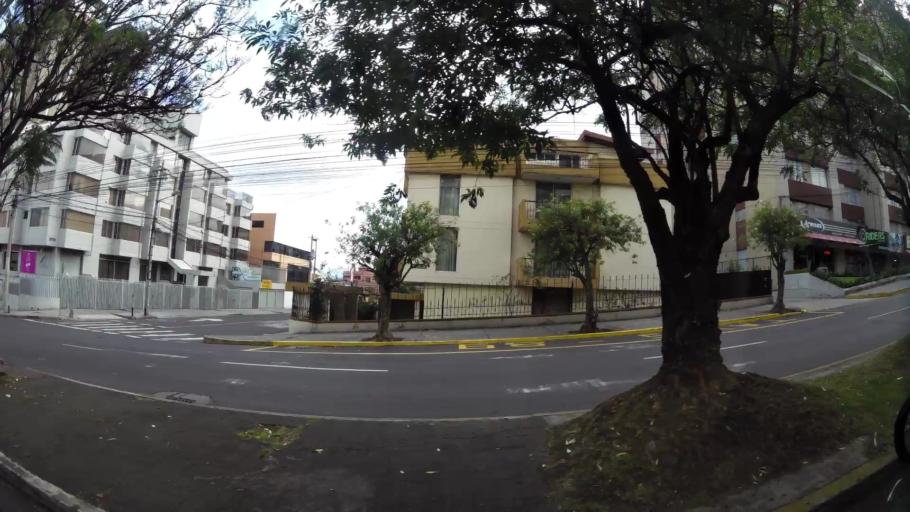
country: EC
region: Pichincha
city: Quito
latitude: -0.1714
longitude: -78.4736
